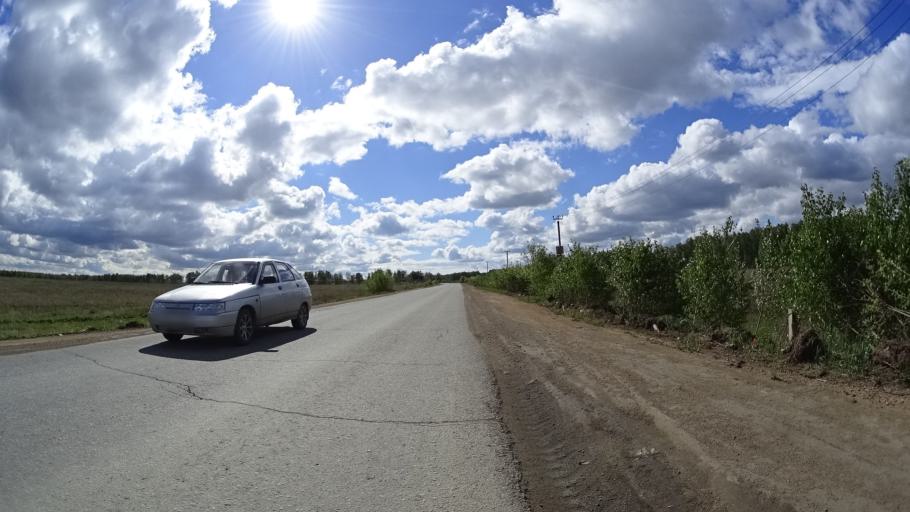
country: RU
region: Chelyabinsk
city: Sargazy
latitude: 55.1426
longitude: 61.2267
